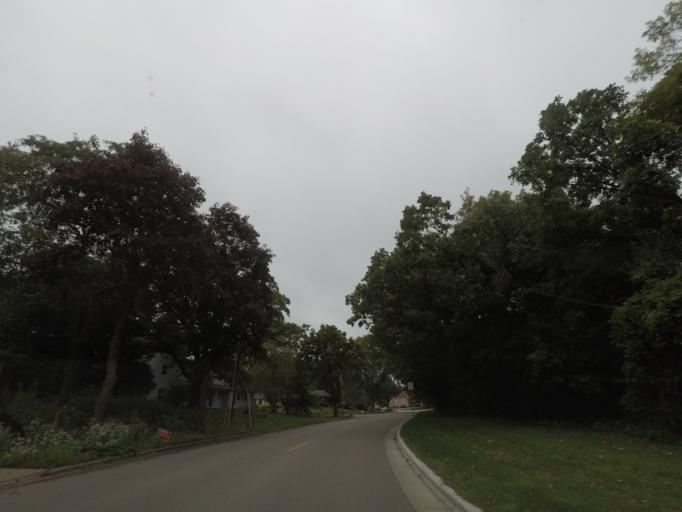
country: US
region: Wisconsin
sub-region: Dane County
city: Middleton
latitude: 43.0643
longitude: -89.4852
